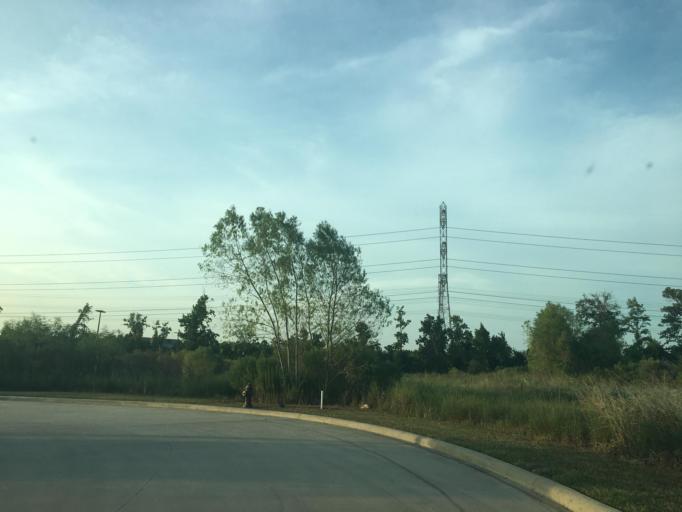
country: US
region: Texas
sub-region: Harris County
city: Spring
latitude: 30.0848
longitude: -95.4471
